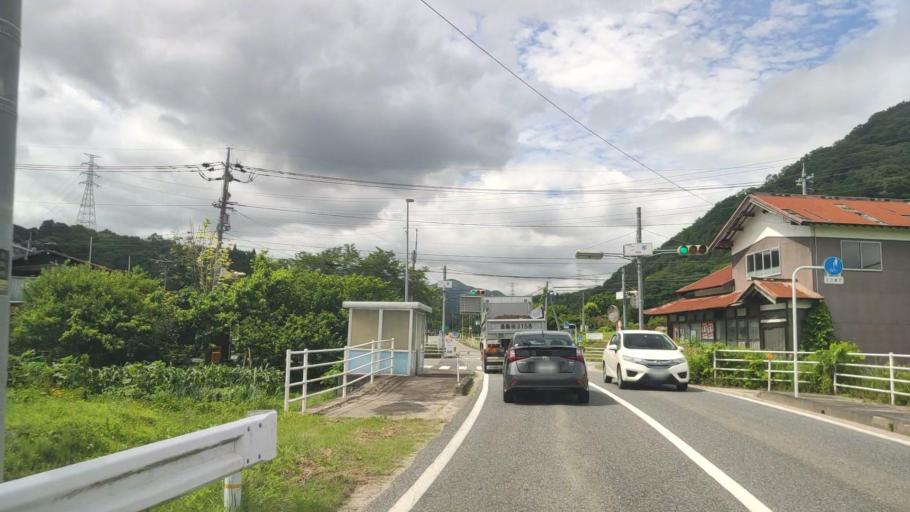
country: JP
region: Tottori
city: Yonago
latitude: 35.2978
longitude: 133.4137
